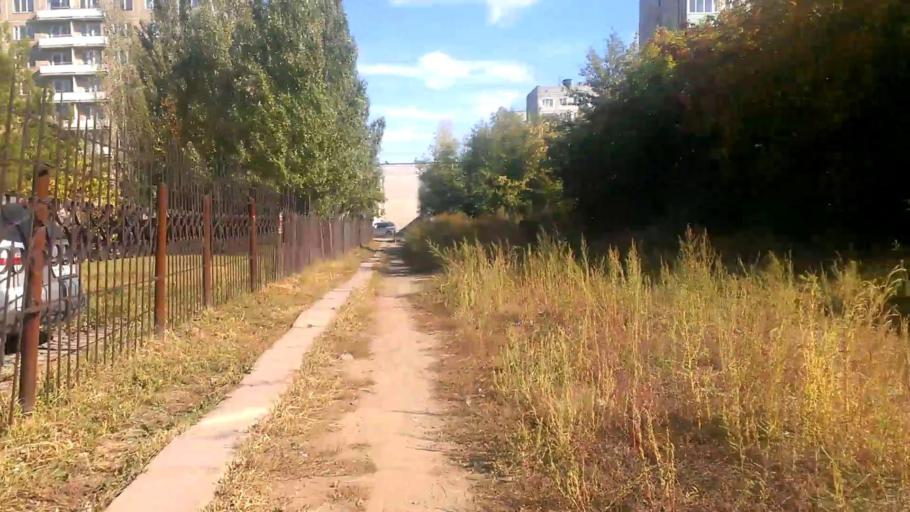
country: RU
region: Altai Krai
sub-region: Gorod Barnaulskiy
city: Barnaul
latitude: 53.3722
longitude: 83.6859
